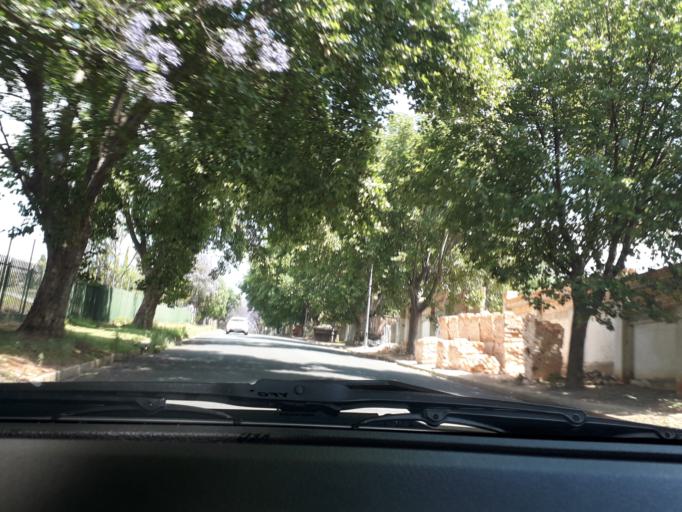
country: ZA
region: Gauteng
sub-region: City of Johannesburg Metropolitan Municipality
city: Johannesburg
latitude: -26.1585
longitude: 28.0672
